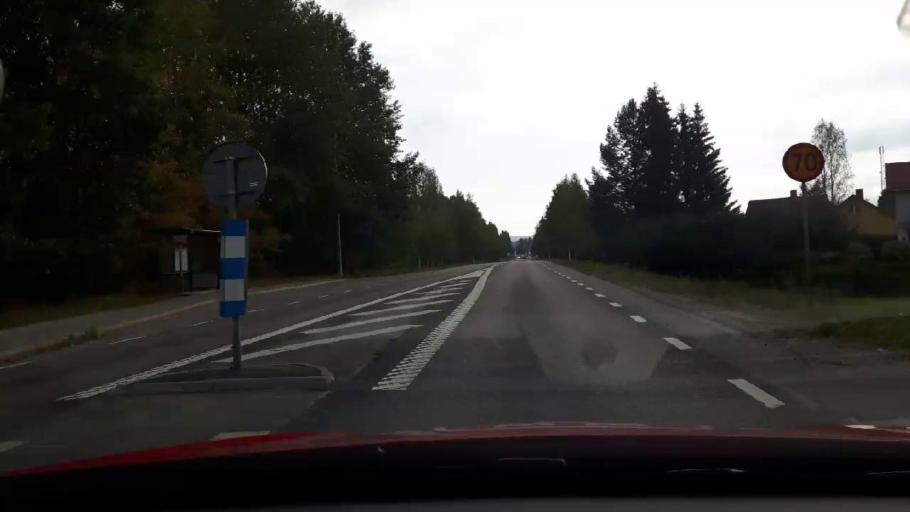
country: SE
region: Gaevleborg
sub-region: Bollnas Kommun
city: Kilafors
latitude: 61.2334
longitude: 16.5585
